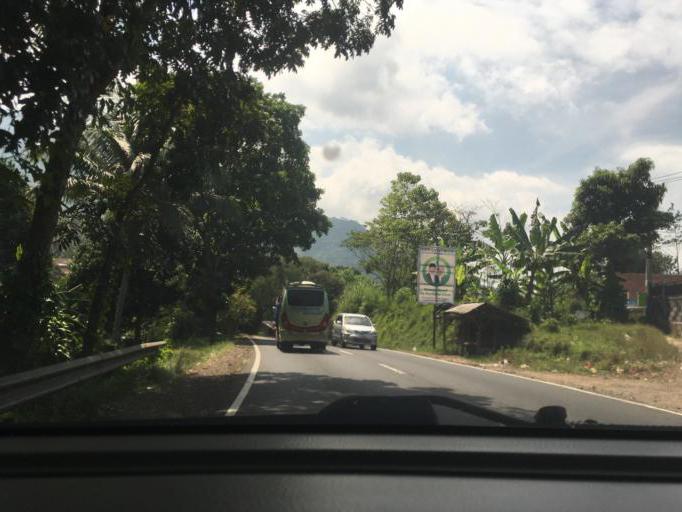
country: ID
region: West Java
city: Wage Cibahayu
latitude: -7.1171
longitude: 108.1179
